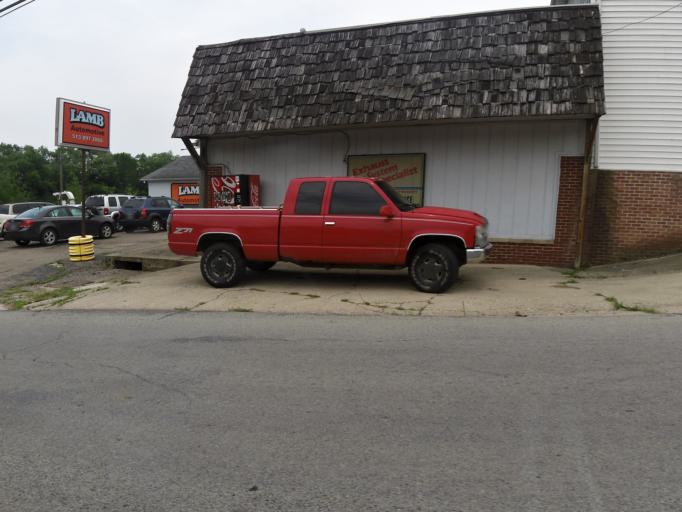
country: US
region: Ohio
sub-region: Warren County
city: Waynesville
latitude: 39.5256
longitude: -84.0788
